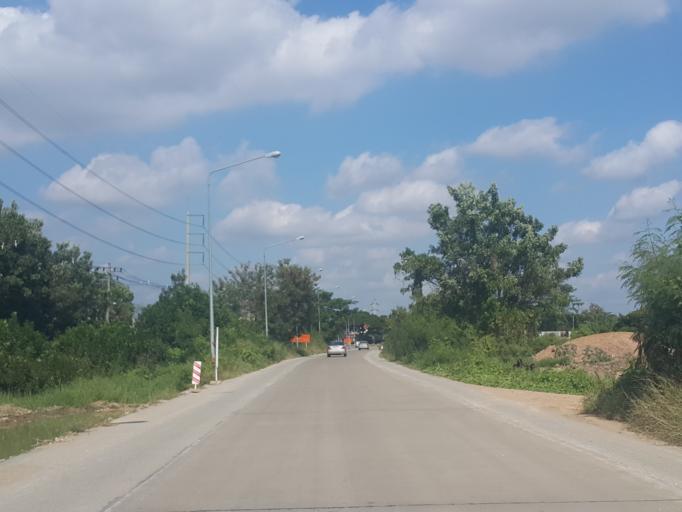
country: TH
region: Chiang Mai
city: Saraphi
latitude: 18.7355
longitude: 99.0349
